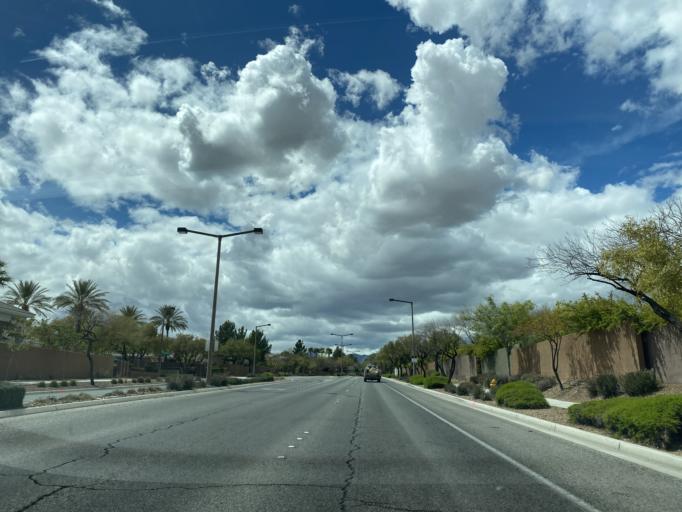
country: US
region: Nevada
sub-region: Clark County
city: Summerlin South
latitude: 36.1677
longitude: -115.3167
